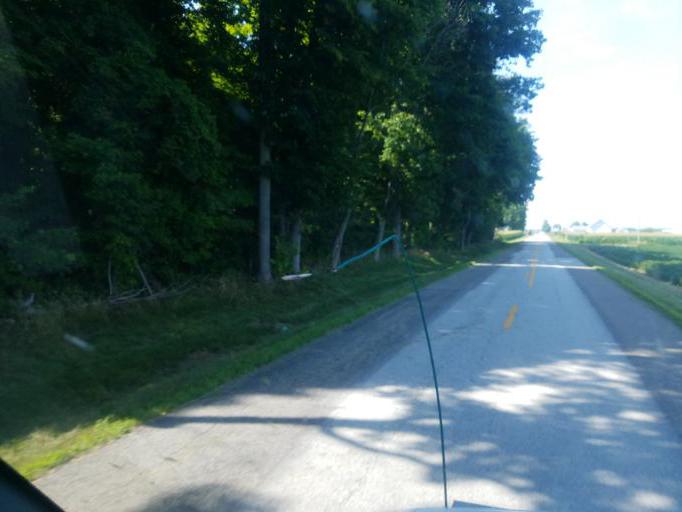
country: US
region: Ohio
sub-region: Shelby County
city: Jackson Center
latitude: 40.5256
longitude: -84.0119
